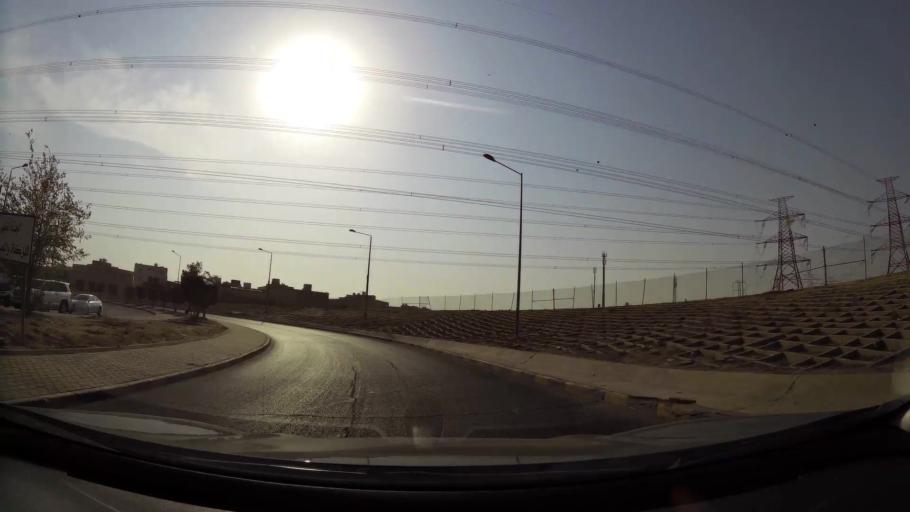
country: KW
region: Mubarak al Kabir
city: Mubarak al Kabir
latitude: 29.1713
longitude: 48.0546
